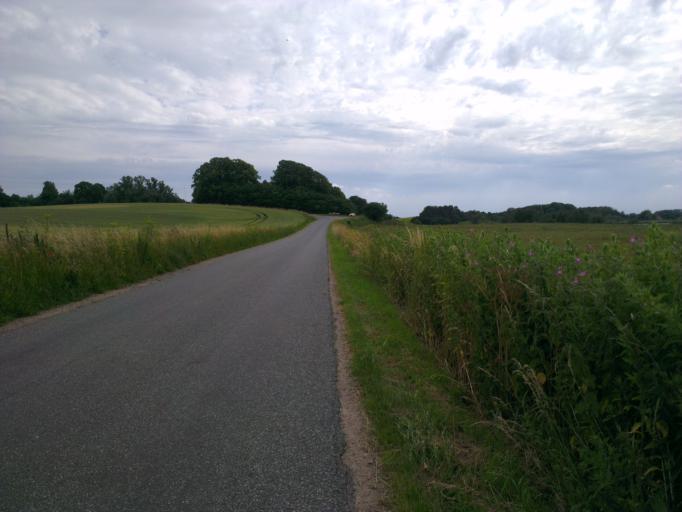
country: DK
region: Capital Region
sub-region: Frederikssund Kommune
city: Skibby
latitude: 55.7459
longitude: 12.0069
